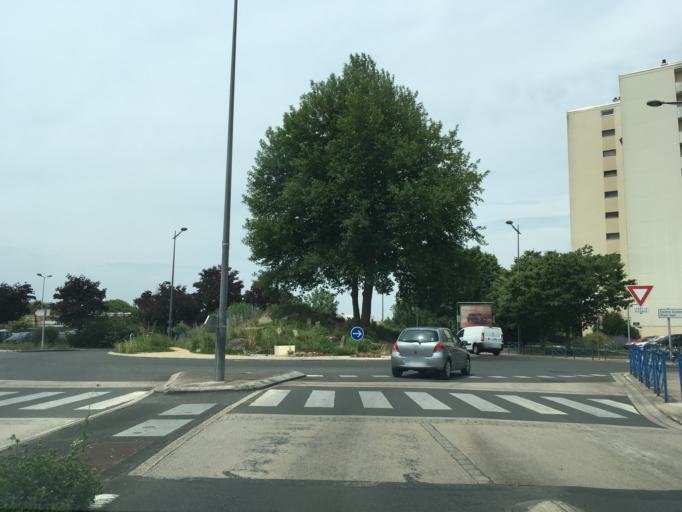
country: FR
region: Poitou-Charentes
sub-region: Departement des Deux-Sevres
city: Niort
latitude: 46.3177
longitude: -0.4843
